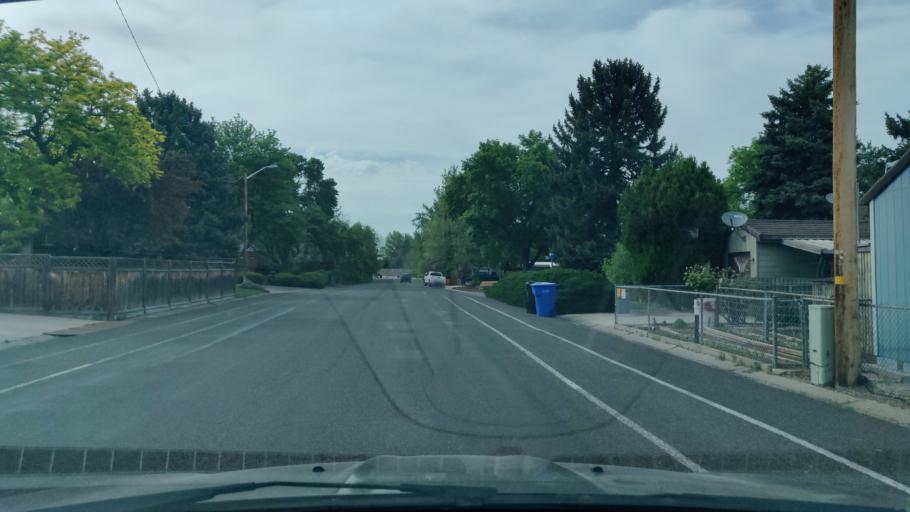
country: US
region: Utah
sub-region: Salt Lake County
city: Little Cottonwood Creek Valley
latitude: 40.6291
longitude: -111.8389
